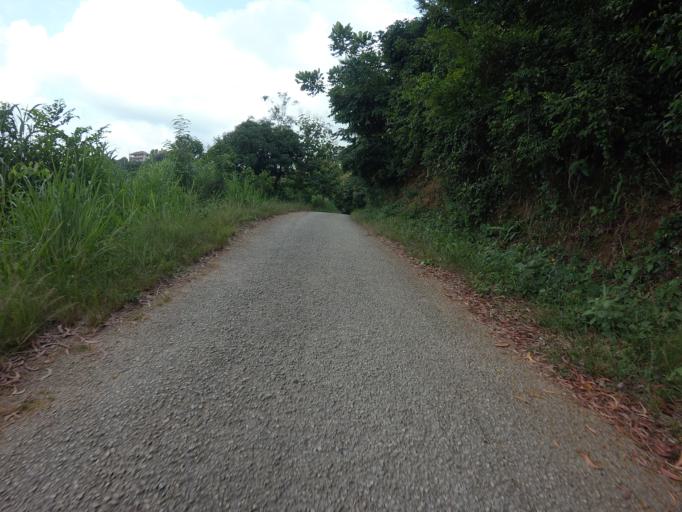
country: TG
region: Plateaux
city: Kpalime
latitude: 6.8885
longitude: 0.4487
